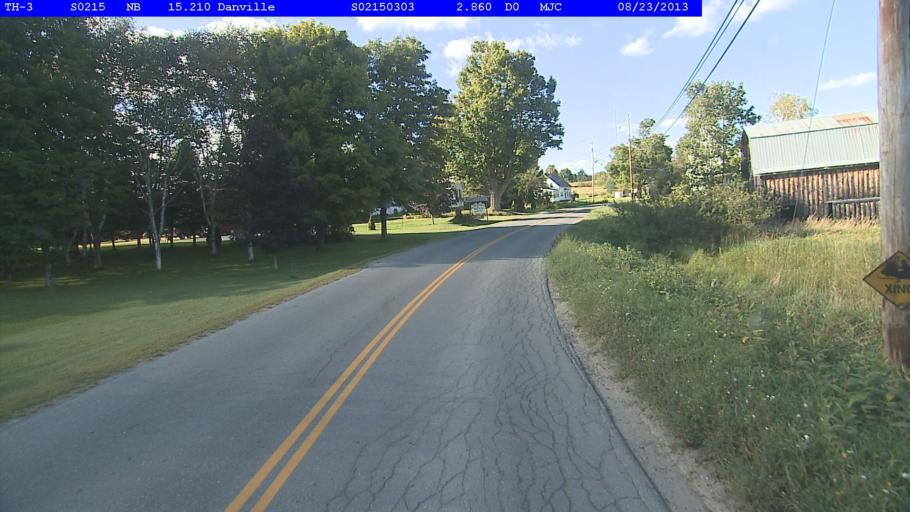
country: US
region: Vermont
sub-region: Caledonia County
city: Saint Johnsbury
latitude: 44.4058
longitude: -72.1416
